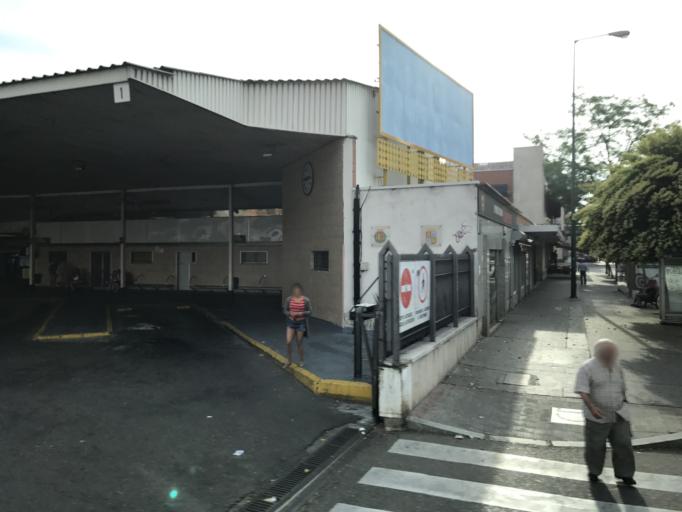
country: ES
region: Castille and Leon
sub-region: Provincia de Valladolid
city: Valladolid
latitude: 41.6412
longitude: -4.7325
